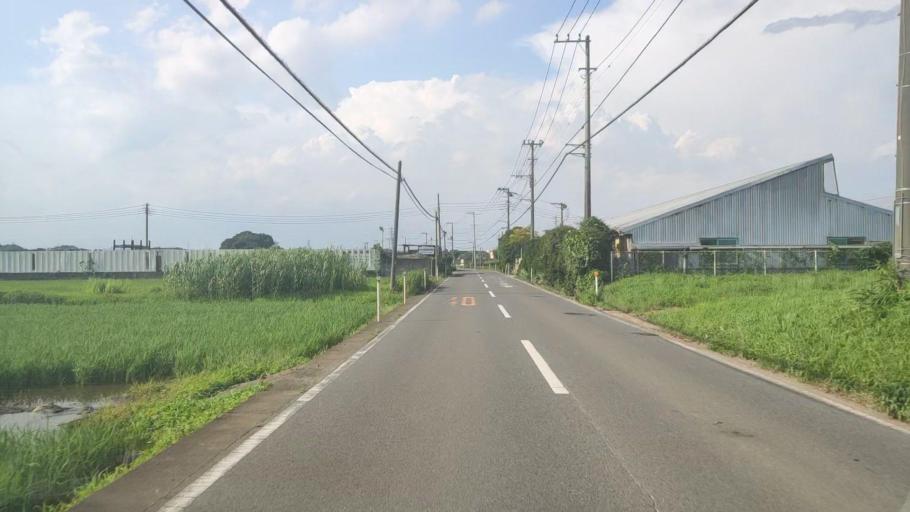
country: JP
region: Kanagawa
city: Isehara
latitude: 35.3666
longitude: 139.3283
